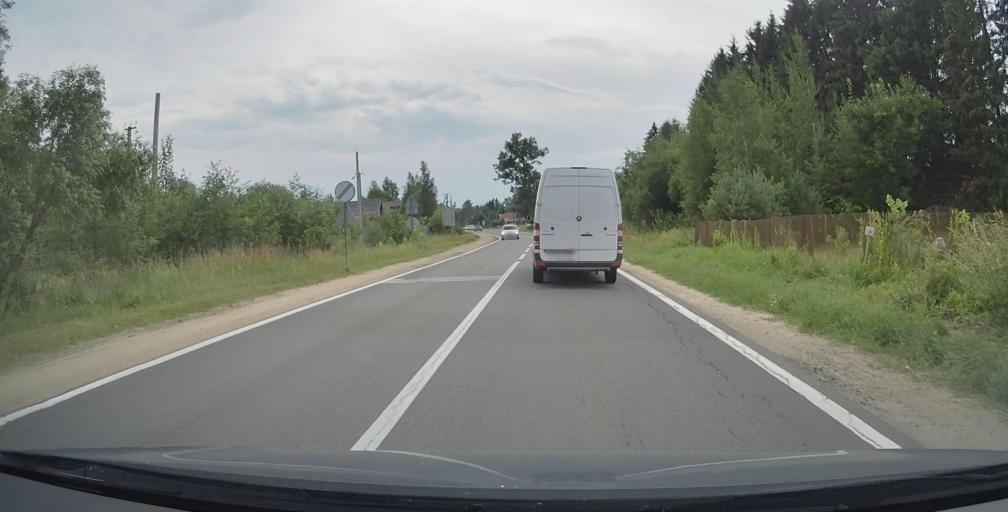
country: RU
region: Jaroslavl
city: Rybinsk
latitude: 57.9767
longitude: 38.7387
